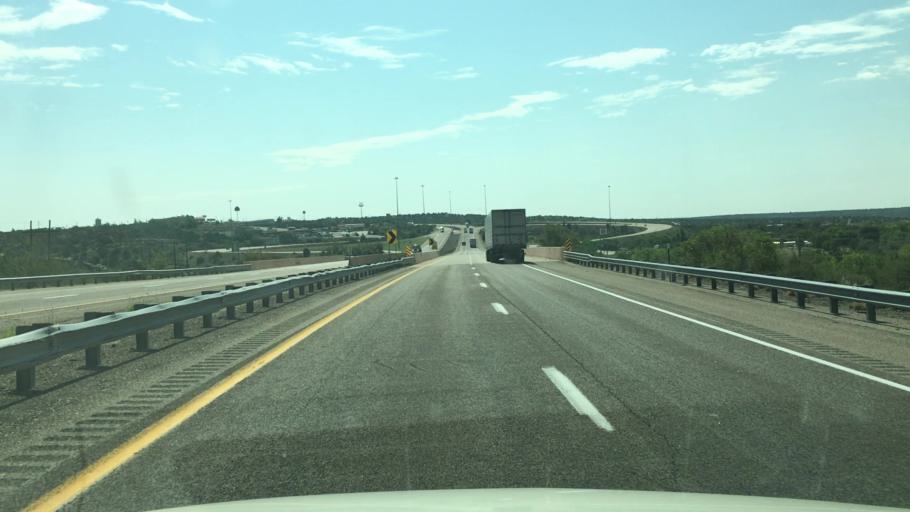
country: US
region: New Mexico
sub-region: Guadalupe County
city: Santa Rosa
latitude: 34.9478
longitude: -104.6796
